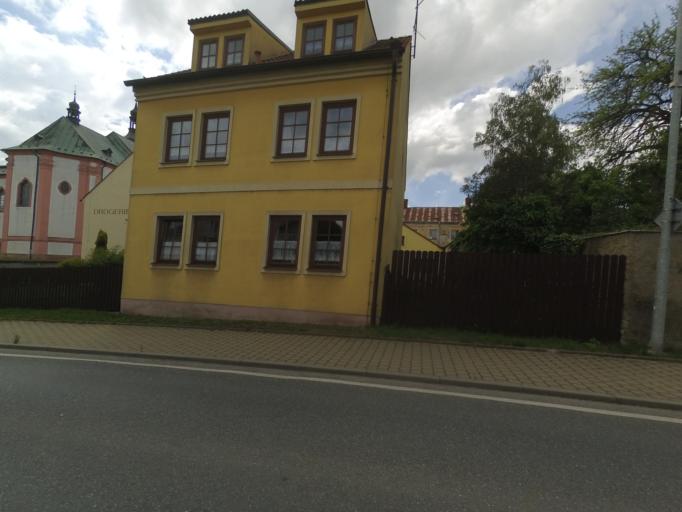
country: CZ
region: Plzensky
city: Bor
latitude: 49.7119
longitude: 12.7774
